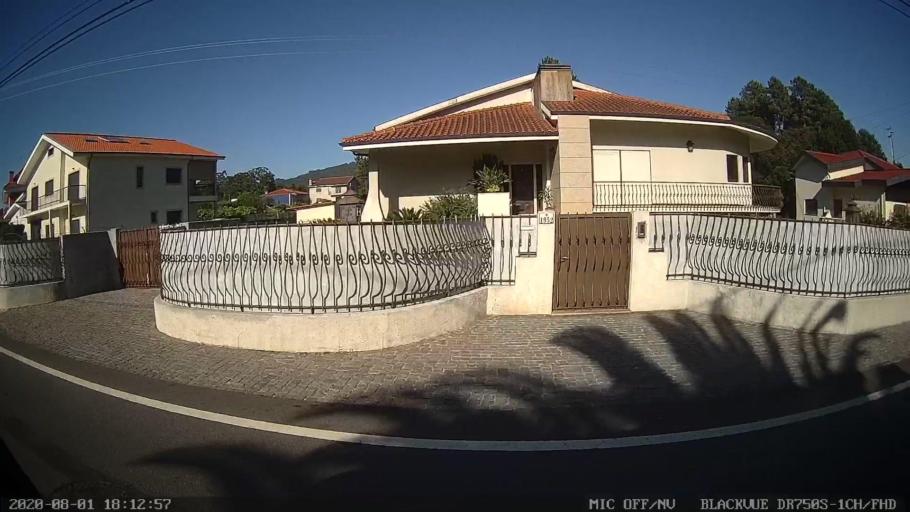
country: PT
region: Porto
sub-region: Santo Tirso
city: Sao Miguel do Couto
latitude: 41.2861
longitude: -8.4720
